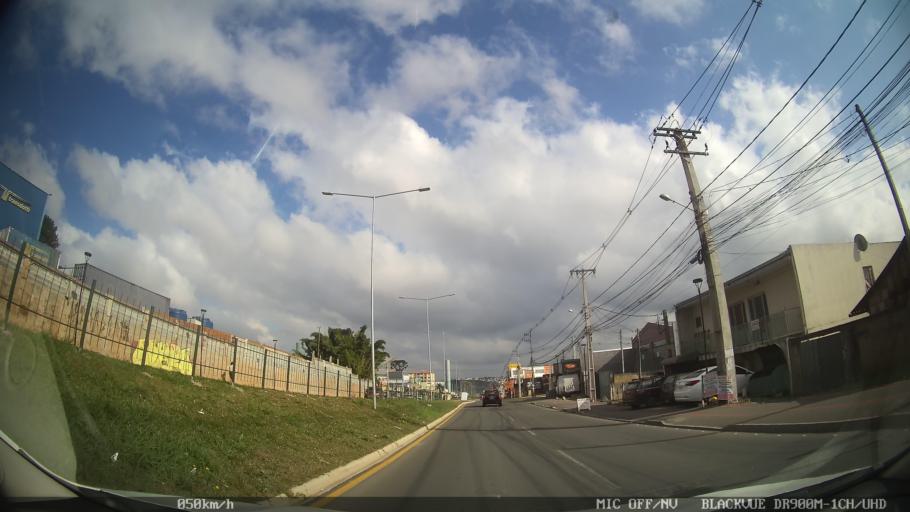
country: BR
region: Parana
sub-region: Pinhais
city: Pinhais
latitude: -25.3827
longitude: -49.1860
